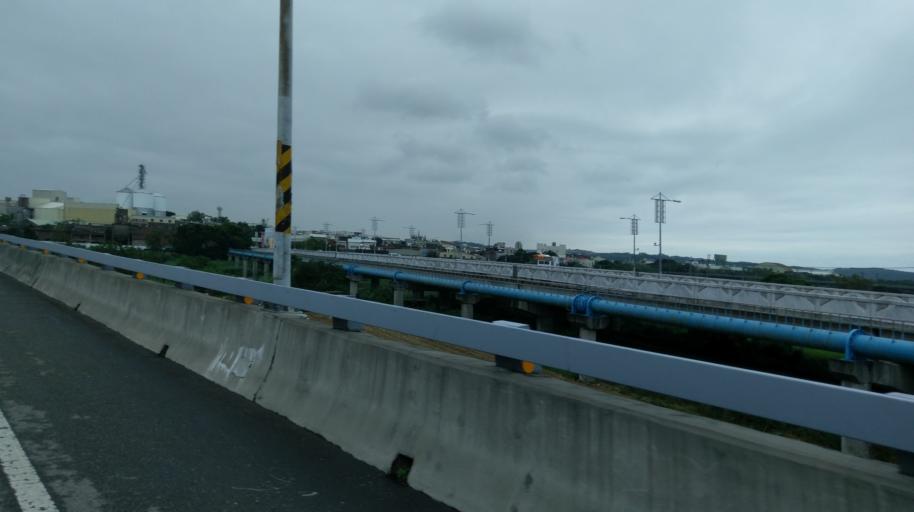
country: TW
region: Taiwan
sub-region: Miaoli
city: Miaoli
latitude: 24.6684
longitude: 120.8827
